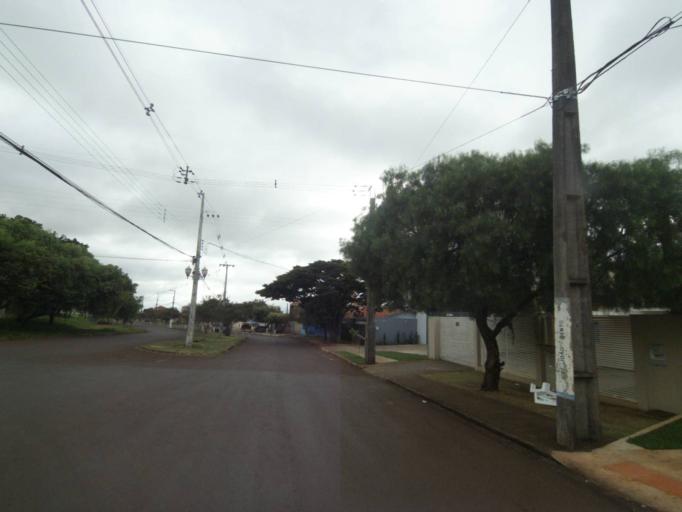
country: BR
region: Parana
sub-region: Campo Mourao
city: Campo Mourao
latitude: -24.0398
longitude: -52.3648
